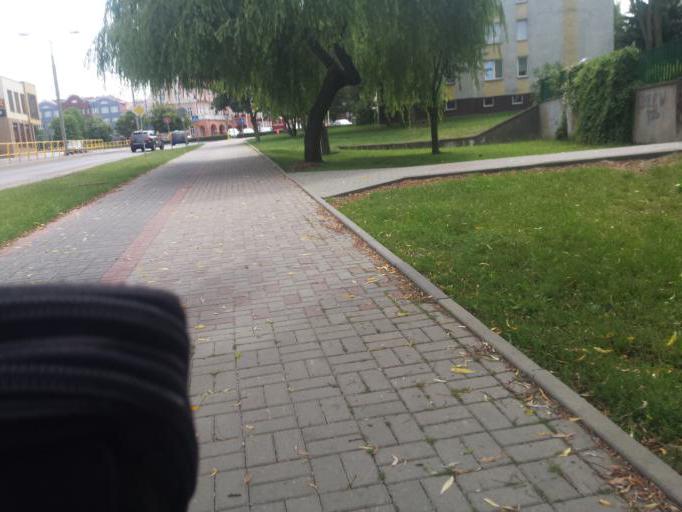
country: PL
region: Warmian-Masurian Voivodeship
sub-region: Powiat ilawski
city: Ilawa
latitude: 53.5985
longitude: 19.5615
